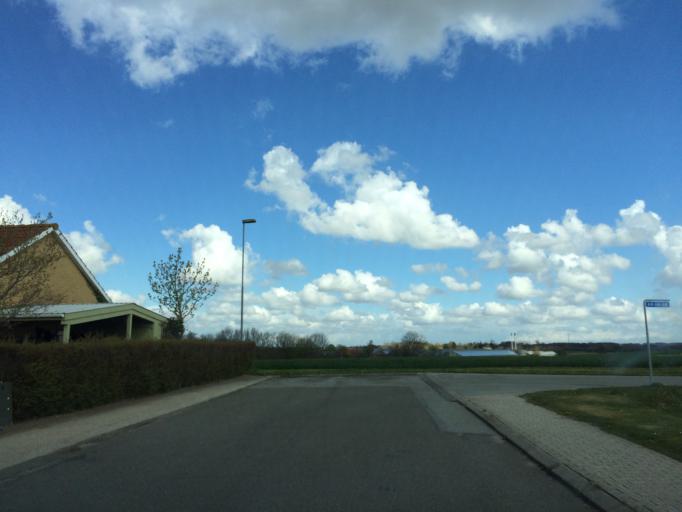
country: DK
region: South Denmark
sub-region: Odense Kommune
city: Bellinge
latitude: 55.2700
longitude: 10.3196
